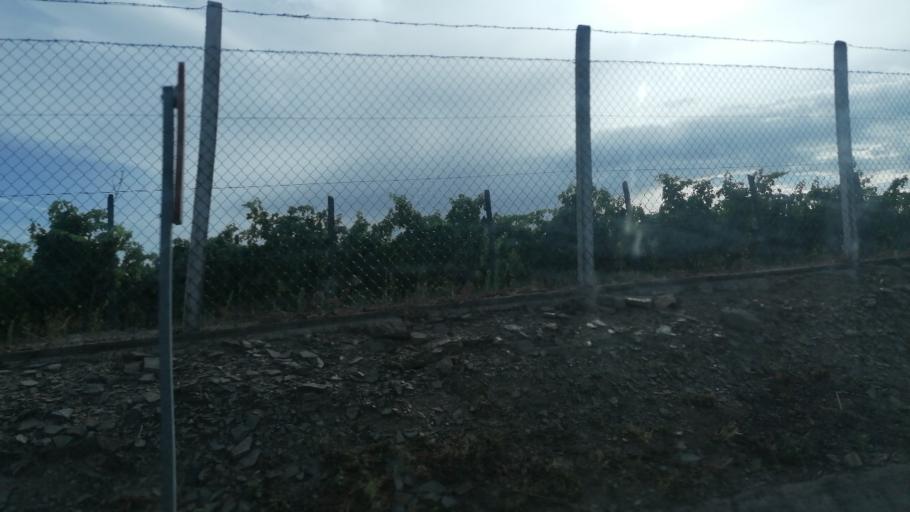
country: PT
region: Viseu
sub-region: Sao Joao da Pesqueira
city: Sao Joao da Pesqueira
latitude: 41.1059
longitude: -7.3875
